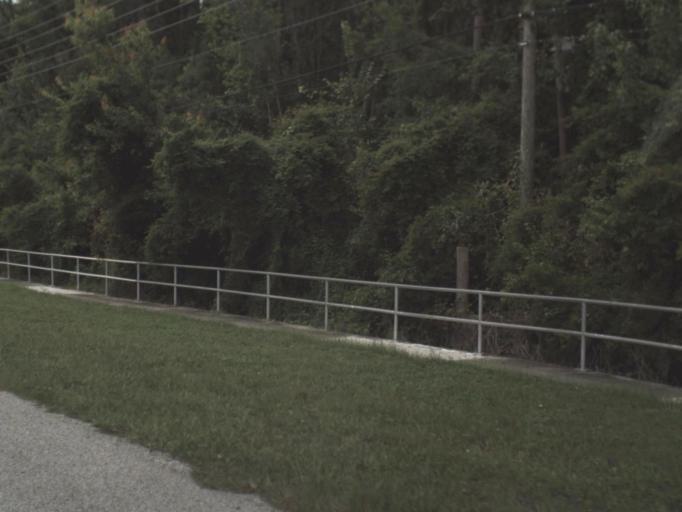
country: US
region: Florida
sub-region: Pasco County
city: Trinity
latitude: 28.1555
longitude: -82.6963
